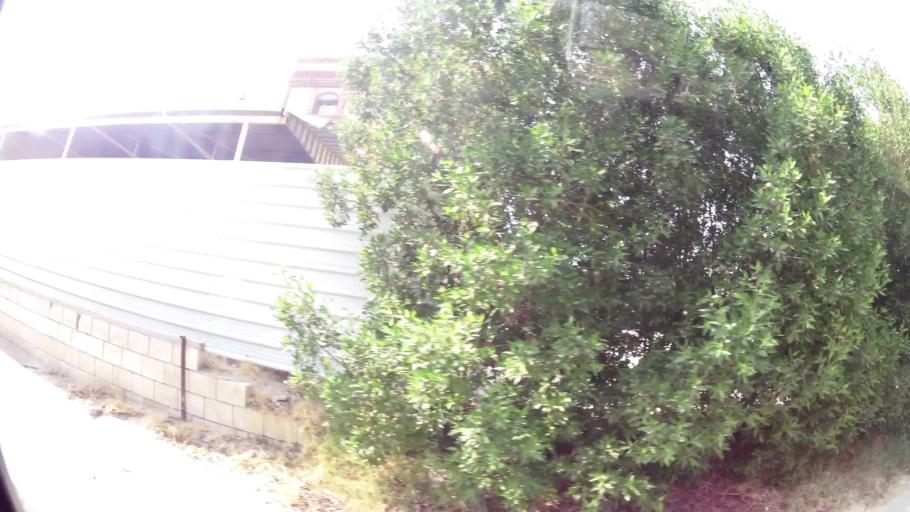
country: KW
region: Muhafazat al Jahra'
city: Al Jahra'
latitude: 29.3285
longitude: 47.6533
